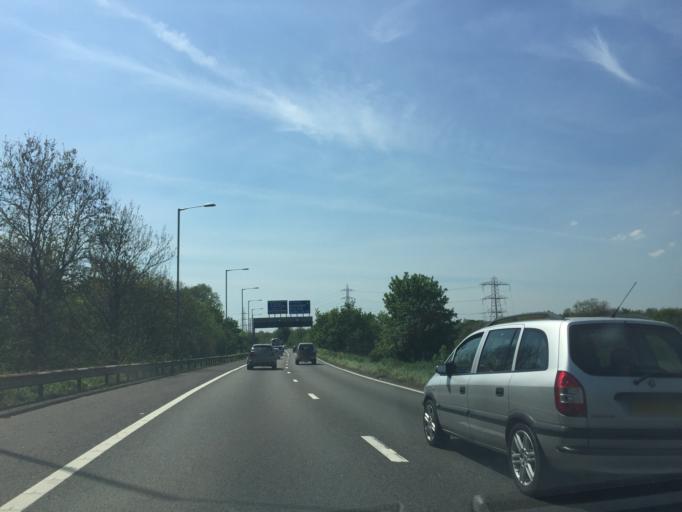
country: GB
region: England
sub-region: Greater London
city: Woodford Green
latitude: 51.5983
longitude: 0.0461
